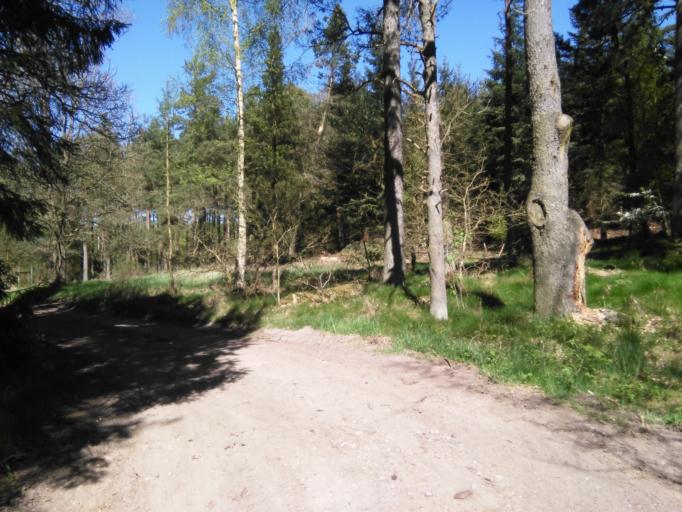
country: DK
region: Central Jutland
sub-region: Odder Kommune
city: Odder
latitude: 55.8868
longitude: 10.0740
